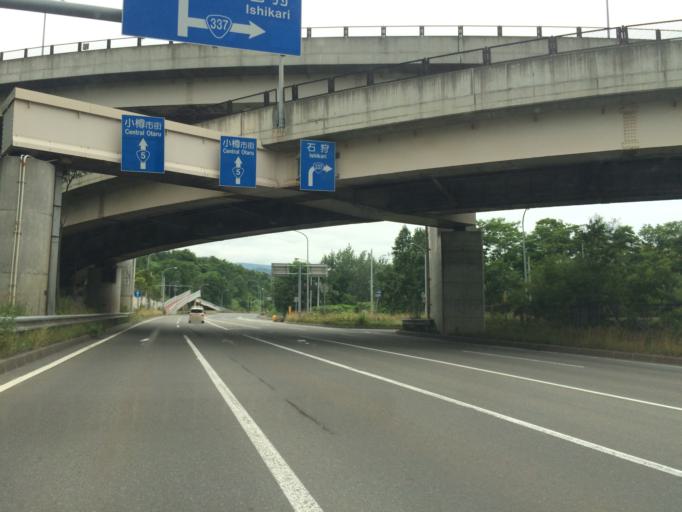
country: JP
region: Hokkaido
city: Sapporo
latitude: 43.1350
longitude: 141.1782
